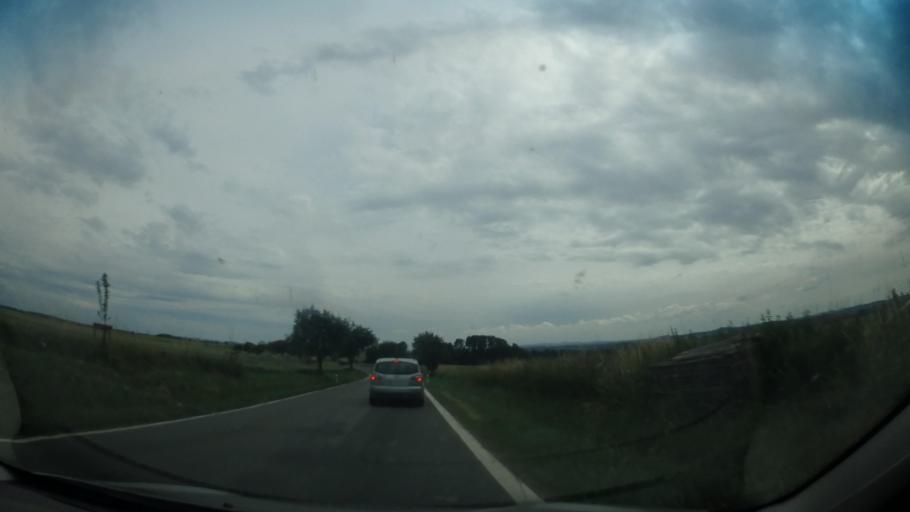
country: CZ
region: Vysocina
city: Bystrice nad Pernstejnem
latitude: 49.5035
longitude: 16.1708
